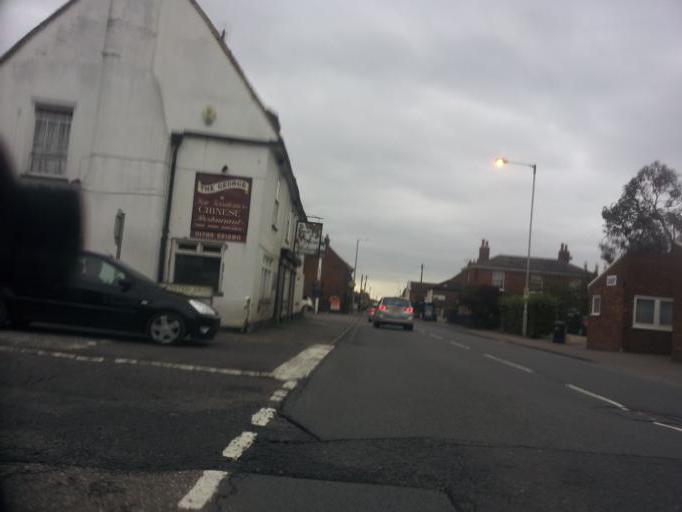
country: GB
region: England
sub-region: Kent
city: Teynham
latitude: 51.3278
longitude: 0.7996
